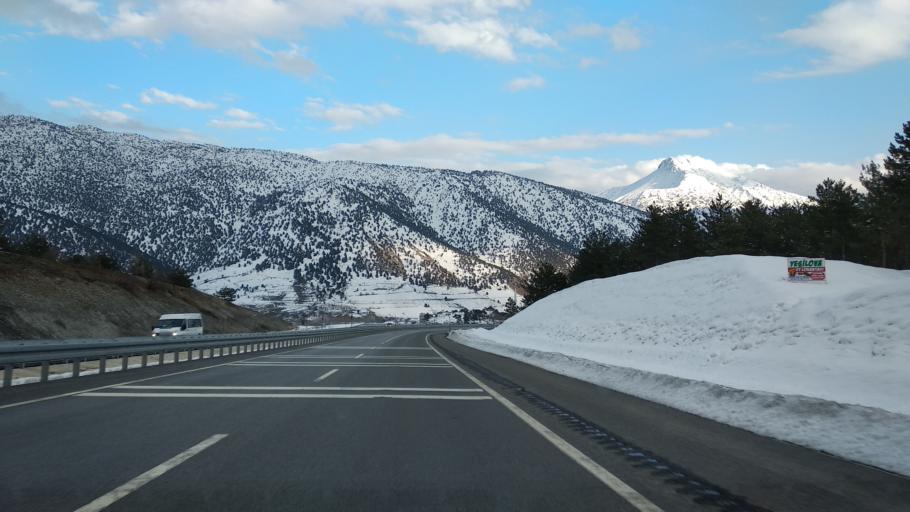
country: TR
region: Kahramanmaras
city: Goksun
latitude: 37.9048
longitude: 36.6042
